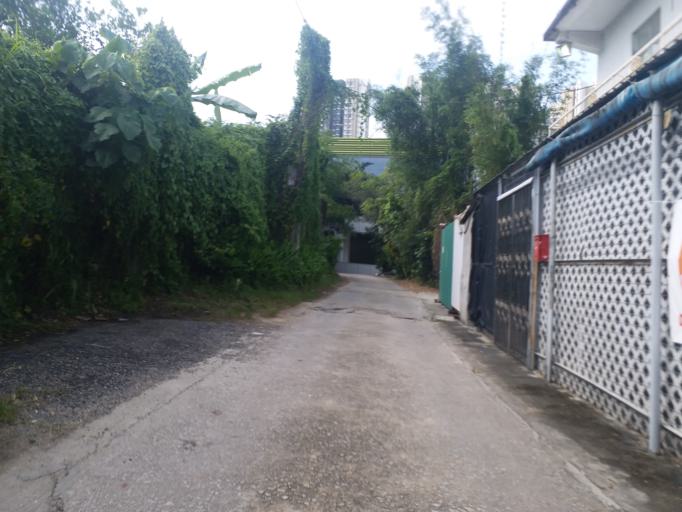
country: HK
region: Yuen Long
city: Yuen Long Kau Hui
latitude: 22.4424
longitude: 114.0035
